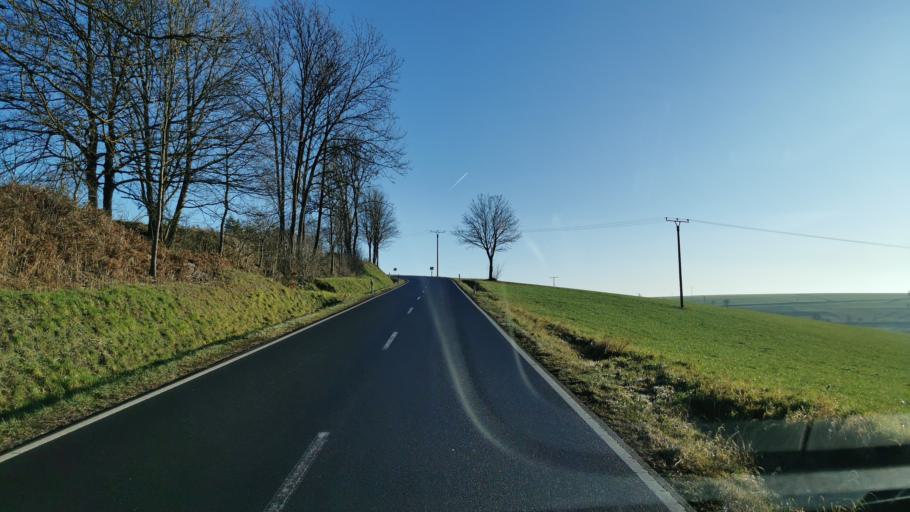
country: DE
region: Rheinland-Pfalz
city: Meisburg
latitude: 50.1080
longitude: 6.6808
